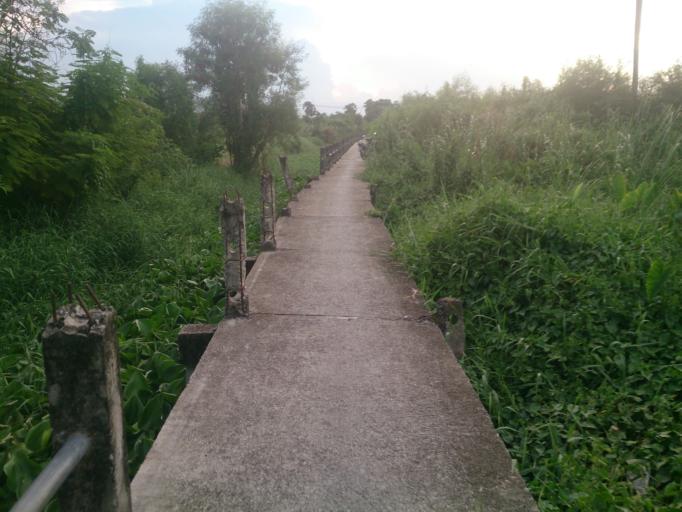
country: TH
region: Nonthaburi
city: Mueang Nonthaburi
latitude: 13.8702
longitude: 100.4986
